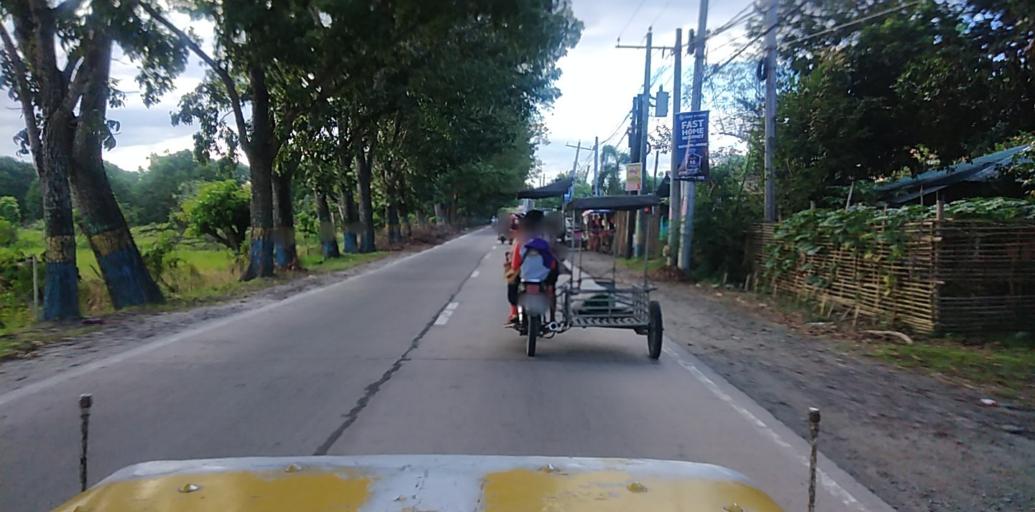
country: PH
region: Central Luzon
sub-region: Province of Pampanga
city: Arayat
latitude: 15.1512
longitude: 120.7439
